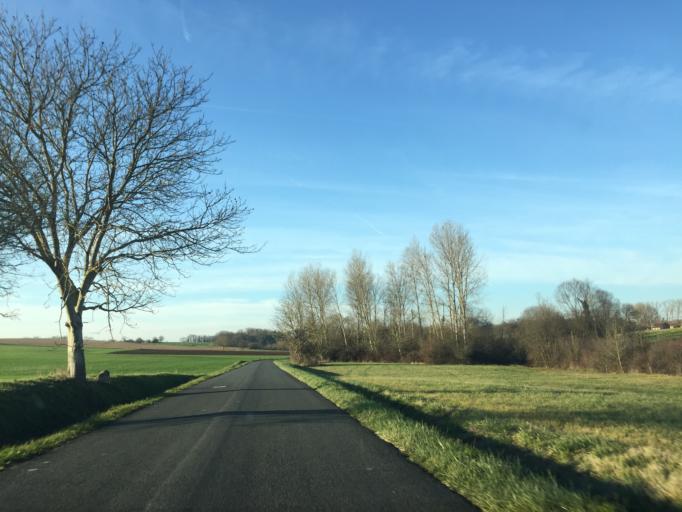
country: FR
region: Aquitaine
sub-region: Departement de la Dordogne
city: Saint-Aulaye
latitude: 45.2451
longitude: 0.2209
